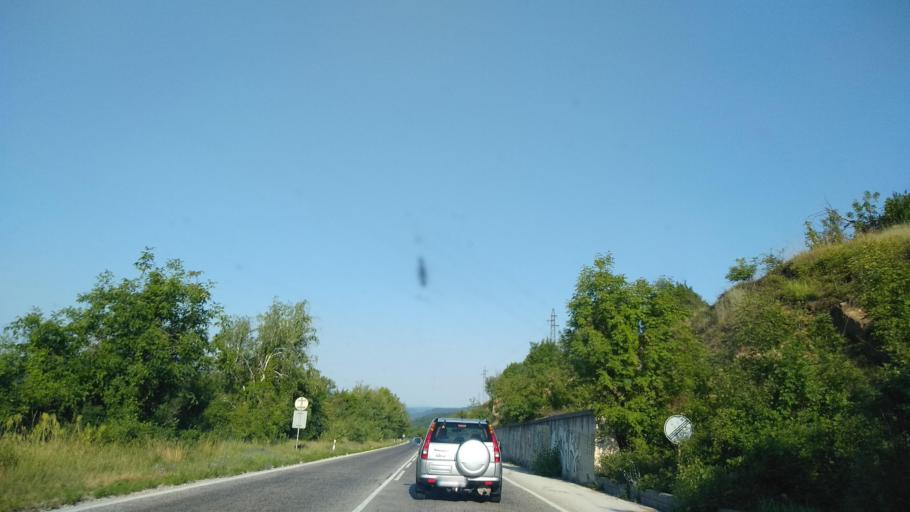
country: BG
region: Lovech
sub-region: Obshtina Lovech
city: Lovech
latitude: 43.0480
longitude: 24.7754
